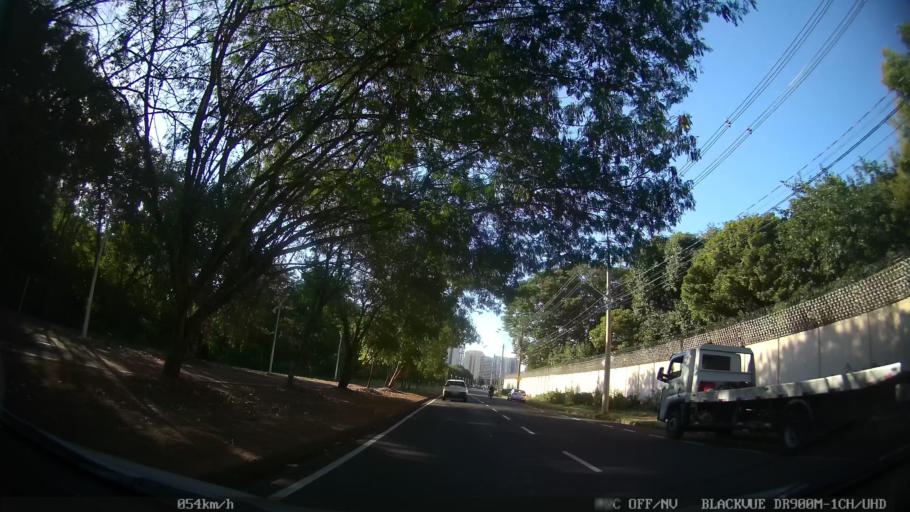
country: BR
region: Sao Paulo
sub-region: Sao Jose Do Rio Preto
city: Sao Jose do Rio Preto
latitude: -20.8452
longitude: -49.4116
